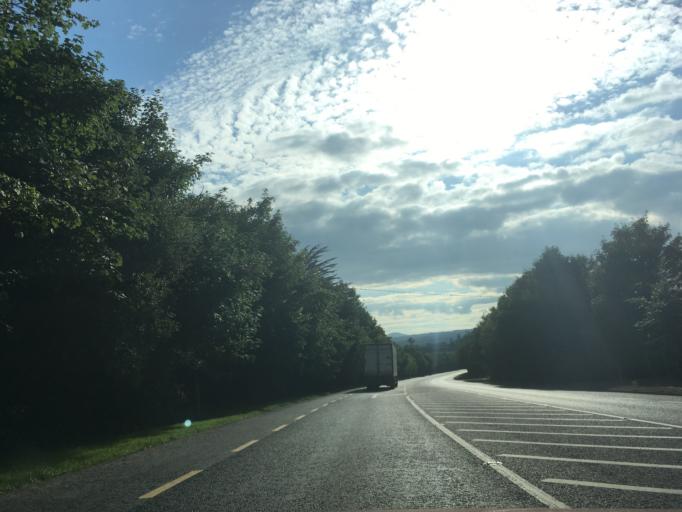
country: IE
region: Leinster
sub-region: Loch Garman
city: New Ross
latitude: 52.3824
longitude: -6.9338
